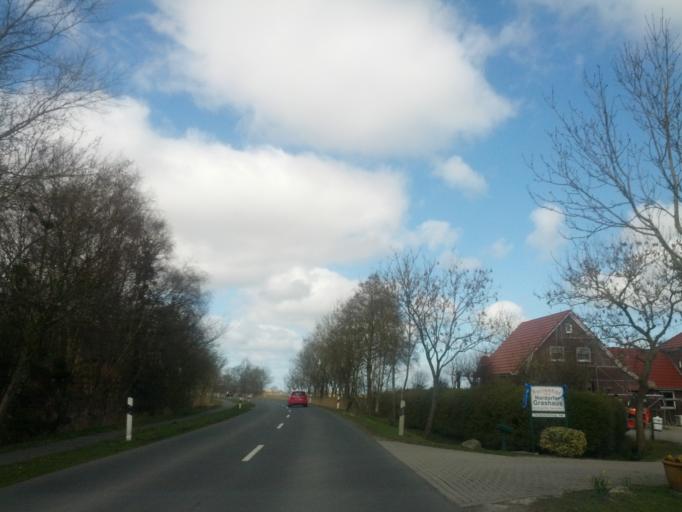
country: DE
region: Lower Saxony
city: Esens
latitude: 53.6618
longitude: 7.6025
